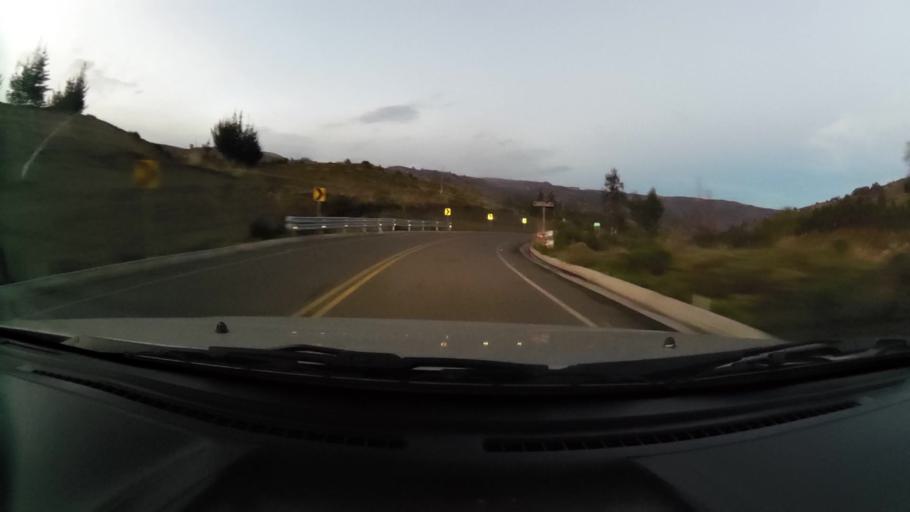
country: EC
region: Chimborazo
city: Riobamba
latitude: -1.8976
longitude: -78.6903
